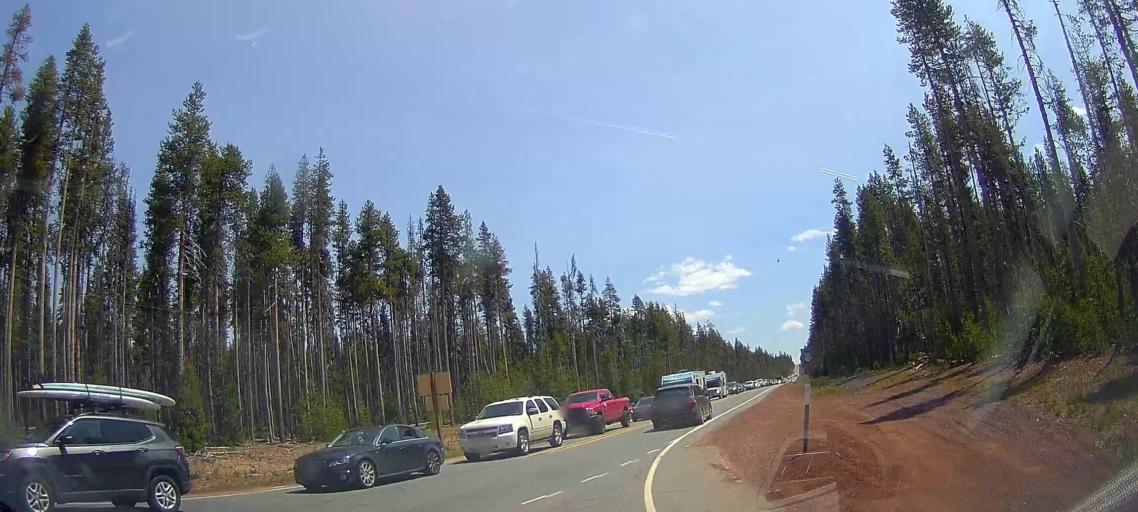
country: US
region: Oregon
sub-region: Lane County
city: Oakridge
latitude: 43.0889
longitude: -122.1162
